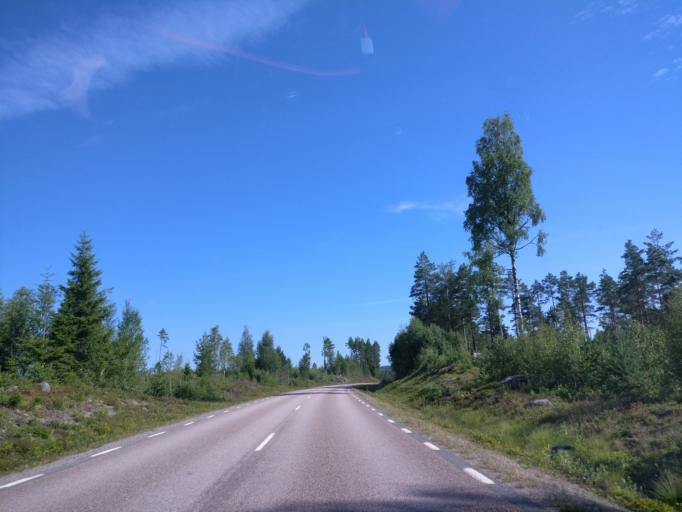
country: SE
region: Vaermland
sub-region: Hagfors Kommun
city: Hagfors
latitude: 60.0365
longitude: 13.9205
